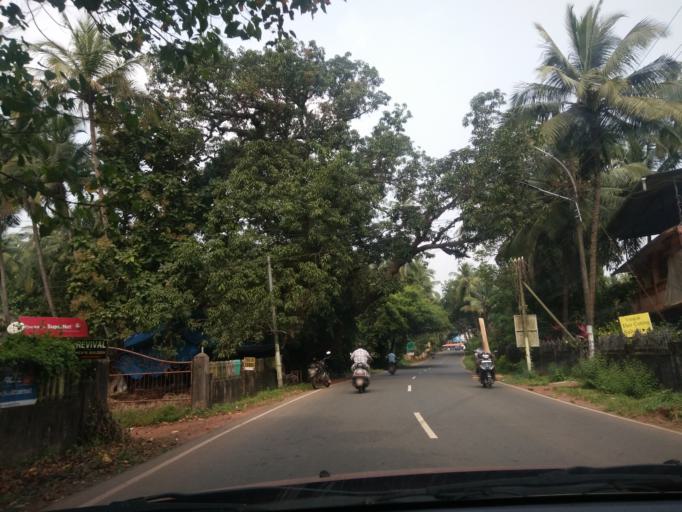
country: IN
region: Goa
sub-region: North Goa
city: Goa Velha
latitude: 15.4375
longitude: 73.8919
